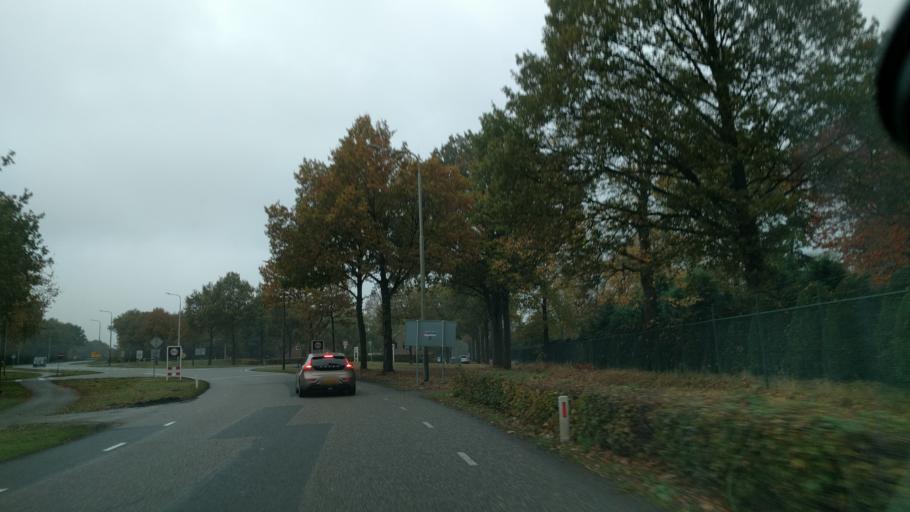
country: NL
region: North Brabant
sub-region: Gemeente Rucphen
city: Rucphen
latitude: 51.5485
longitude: 4.5470
